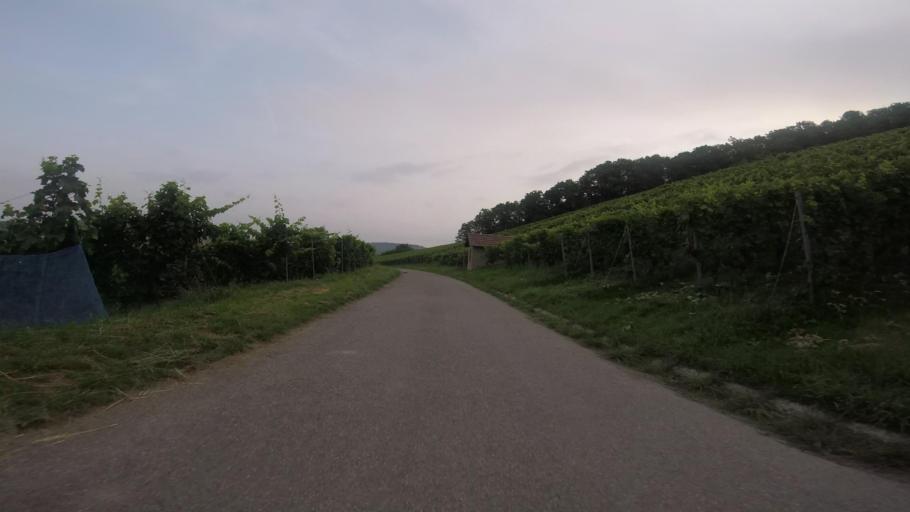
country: DE
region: Baden-Wuerttemberg
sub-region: Regierungsbezirk Stuttgart
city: Oberstenfeld
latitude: 49.0133
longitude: 9.3236
